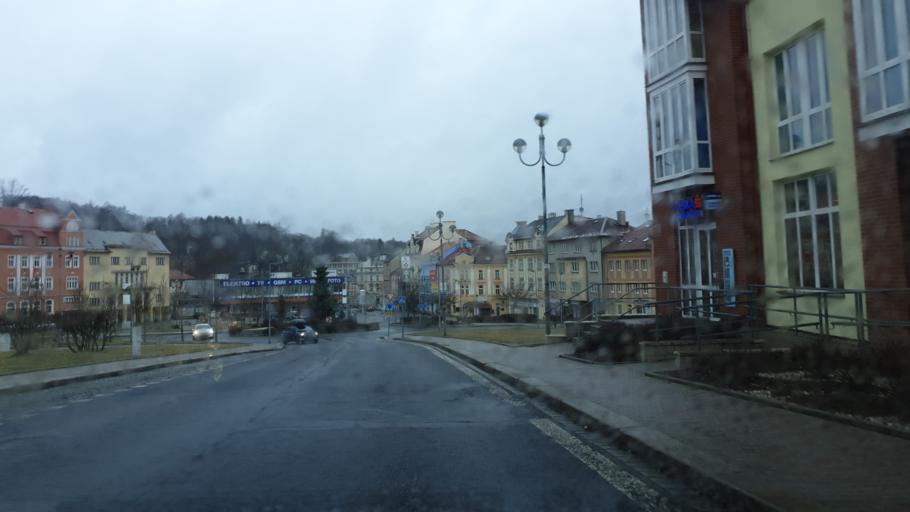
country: CZ
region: Karlovarsky
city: As
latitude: 50.2202
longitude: 12.1906
